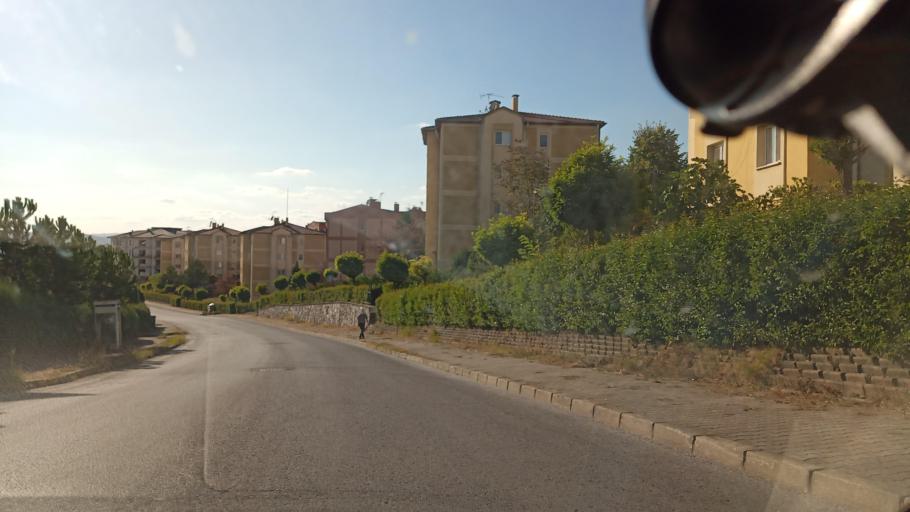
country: TR
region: Kocaeli
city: Kaymaz
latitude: 40.8616
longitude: 30.2893
